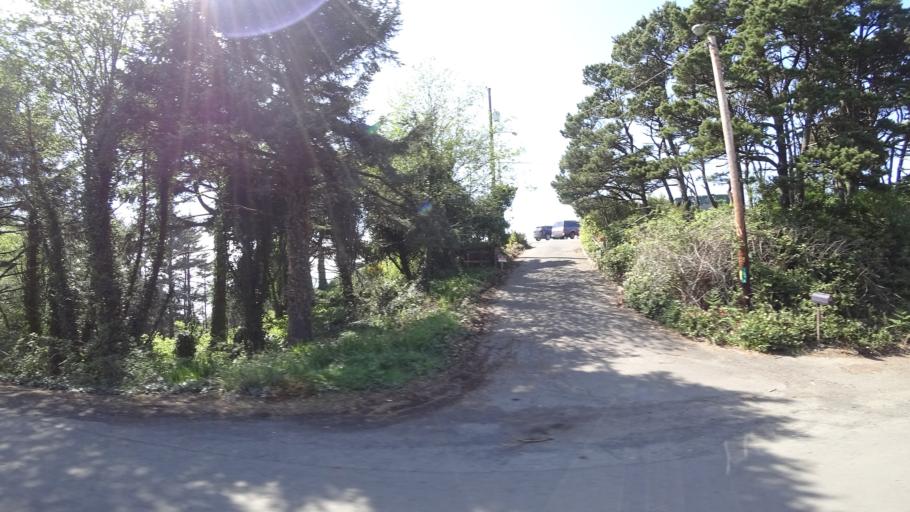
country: US
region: Oregon
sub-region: Lincoln County
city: Newport
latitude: 44.6949
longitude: -124.0626
